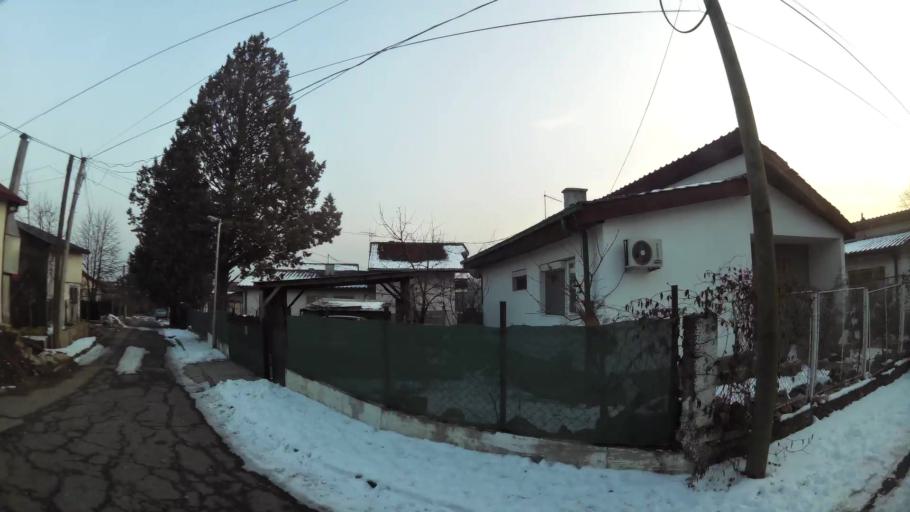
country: MK
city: Creshevo
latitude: 42.0100
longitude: 21.5054
